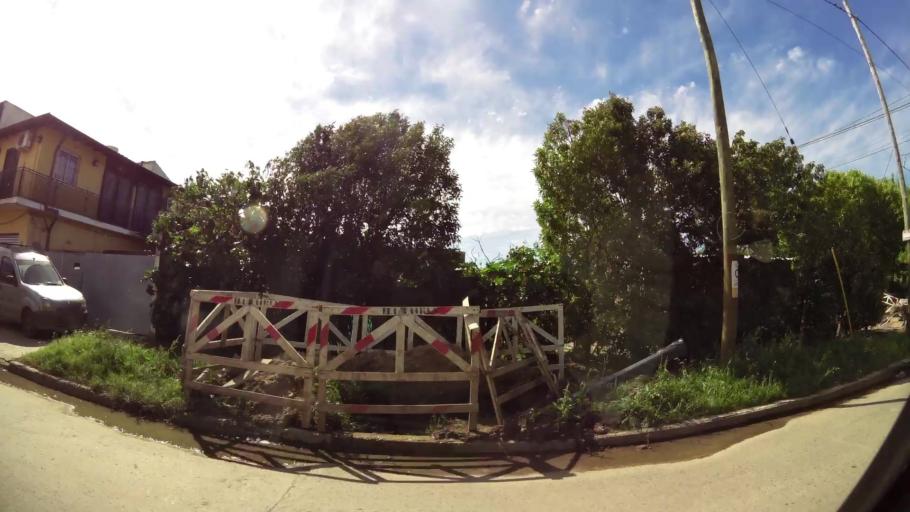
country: AR
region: Buenos Aires
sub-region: Partido de Almirante Brown
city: Adrogue
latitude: -34.7822
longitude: -58.3068
